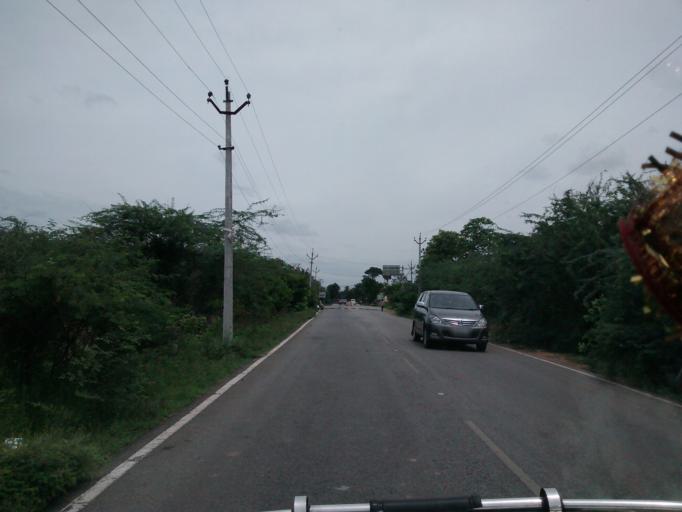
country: IN
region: Andhra Pradesh
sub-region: Chittoor
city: Narasingapuram
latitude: 13.6108
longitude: 79.3337
